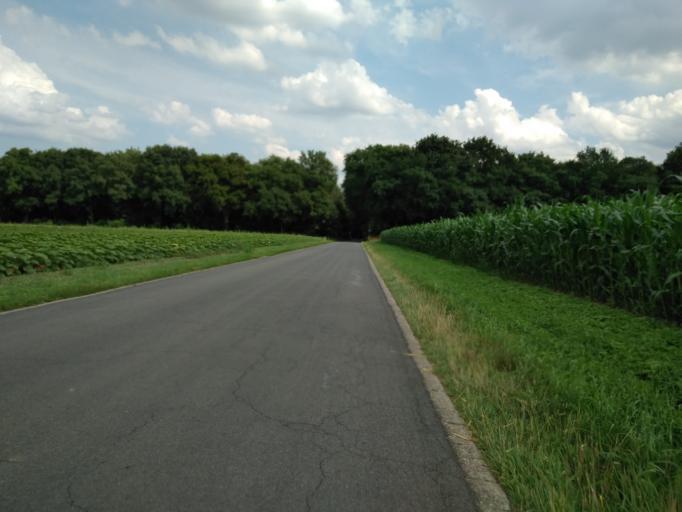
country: DE
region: North Rhine-Westphalia
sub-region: Regierungsbezirk Dusseldorf
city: Schermbeck
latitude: 51.6783
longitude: 6.8923
